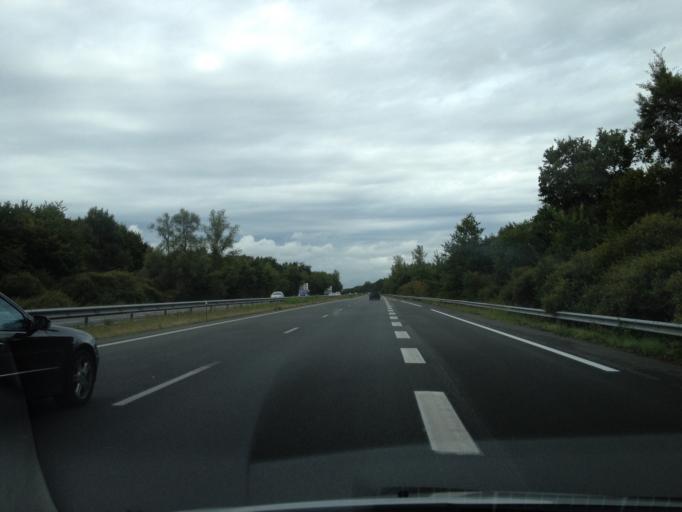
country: FR
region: Aquitaine
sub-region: Departement du Lot-et-Garonne
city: Fourques-sur-Garonne
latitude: 44.4091
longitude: 0.1827
